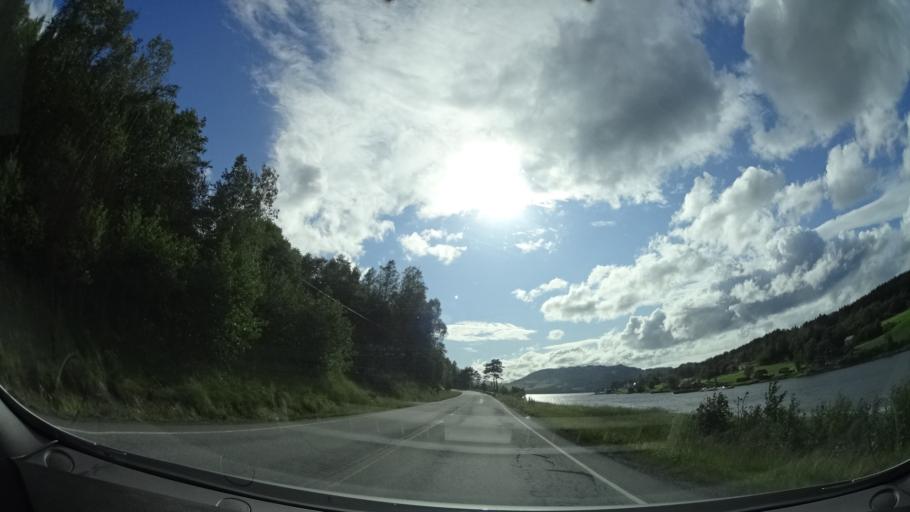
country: NO
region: More og Romsdal
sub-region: Halsa
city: Liaboen
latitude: 63.0856
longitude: 8.3491
